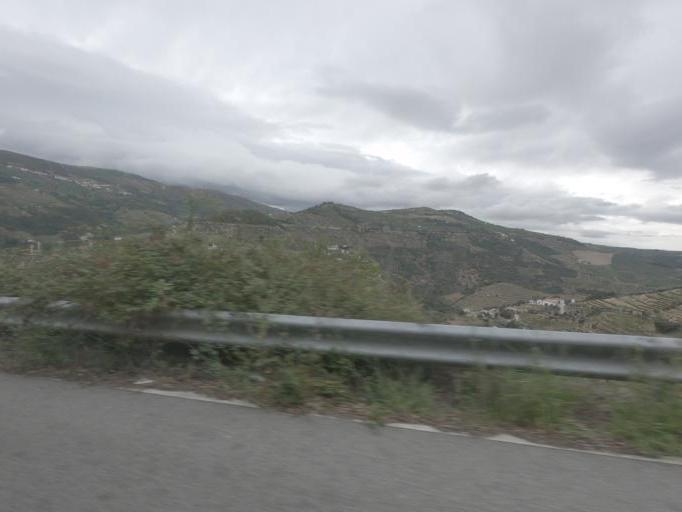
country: PT
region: Vila Real
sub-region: Sabrosa
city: Vilela
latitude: 41.2026
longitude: -7.5364
